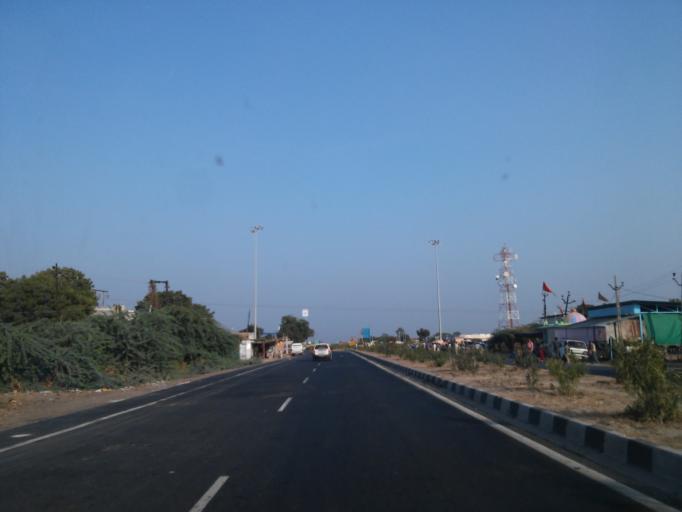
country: IN
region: Gujarat
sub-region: Ahmadabad
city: Mandal
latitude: 23.0980
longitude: 72.0614
